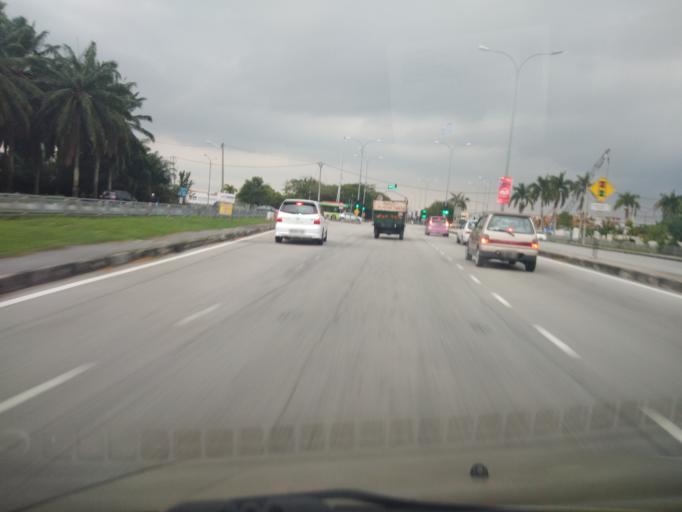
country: MY
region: Penang
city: Tasek Glugor
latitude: 5.5197
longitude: 100.4747
